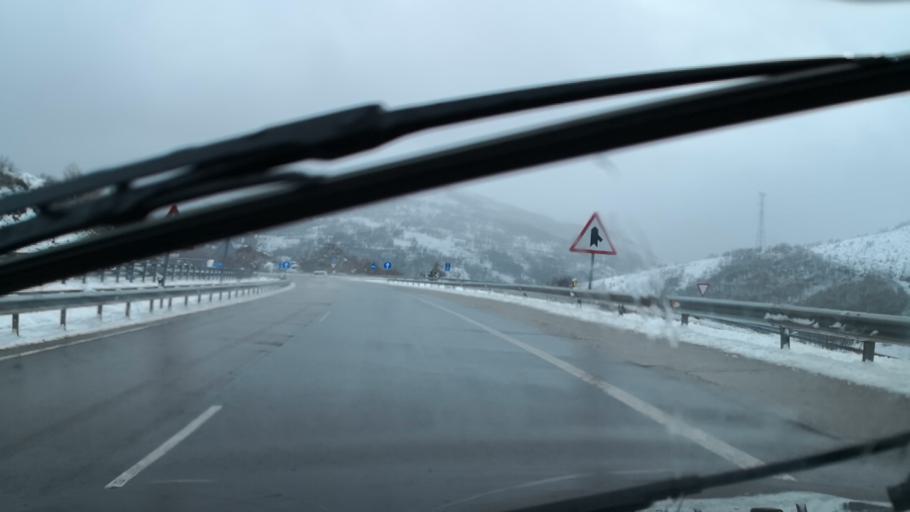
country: ES
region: Castille and Leon
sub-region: Provincia de Zamora
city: Lubian
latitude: 42.0354
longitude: -6.9342
